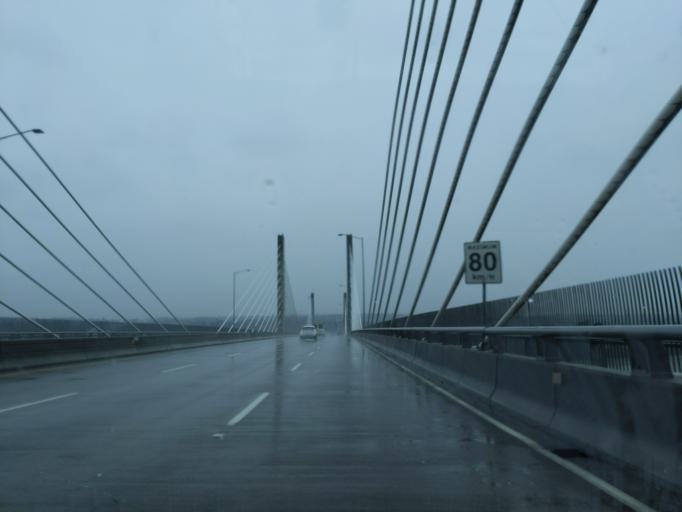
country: CA
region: British Columbia
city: Pitt Meadows
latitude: 49.1966
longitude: -122.6658
